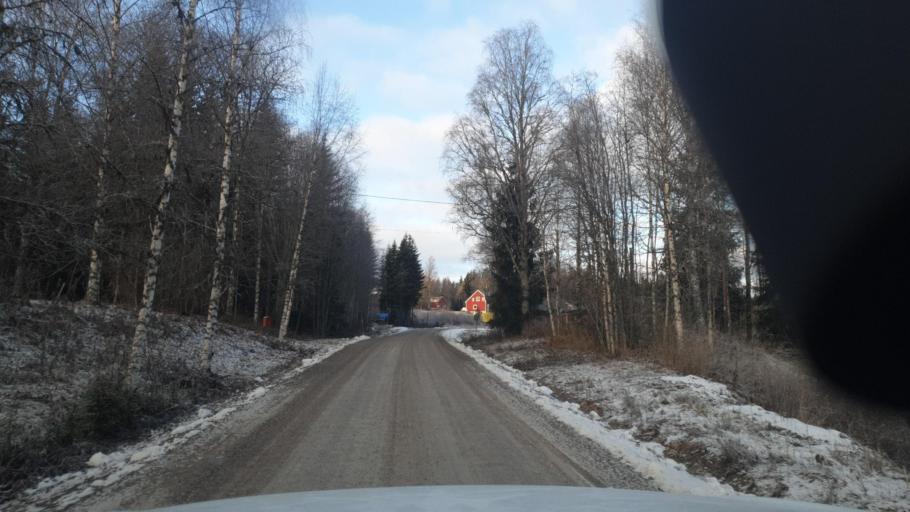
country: SE
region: Vaermland
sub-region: Eda Kommun
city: Charlottenberg
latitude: 60.0921
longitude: 12.4977
